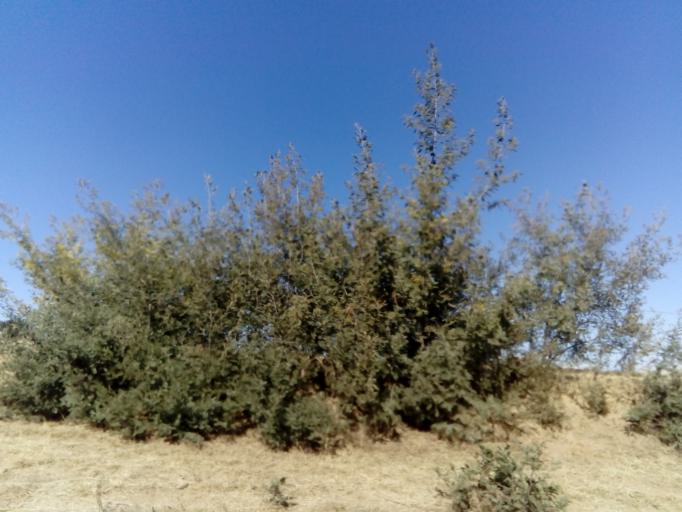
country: LS
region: Berea
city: Teyateyaneng
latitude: -29.1288
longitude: 27.8369
